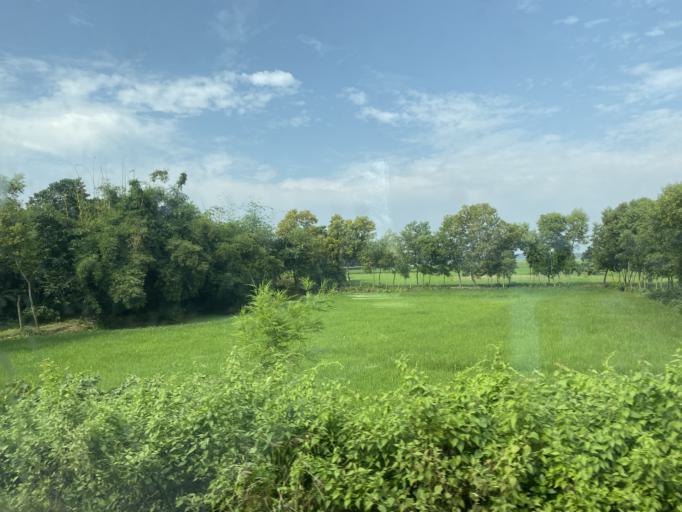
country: IN
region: Tripura
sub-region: West Tripura
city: Agartala
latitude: 23.9896
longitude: 91.2845
